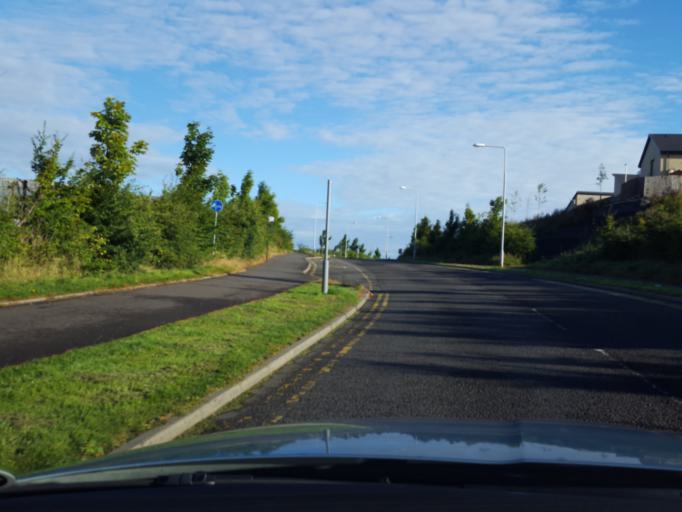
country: GB
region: Scotland
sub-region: Fife
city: Crossgates
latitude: 56.0764
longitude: -3.4050
